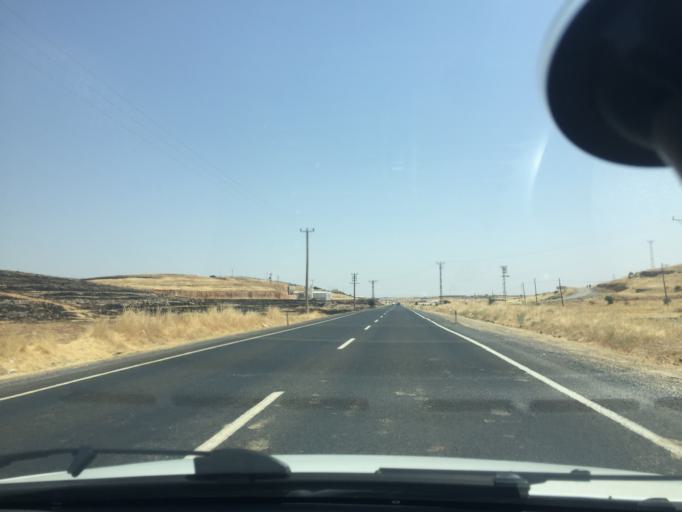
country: TR
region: Mardin
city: Kindirip
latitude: 37.4603
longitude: 41.2357
